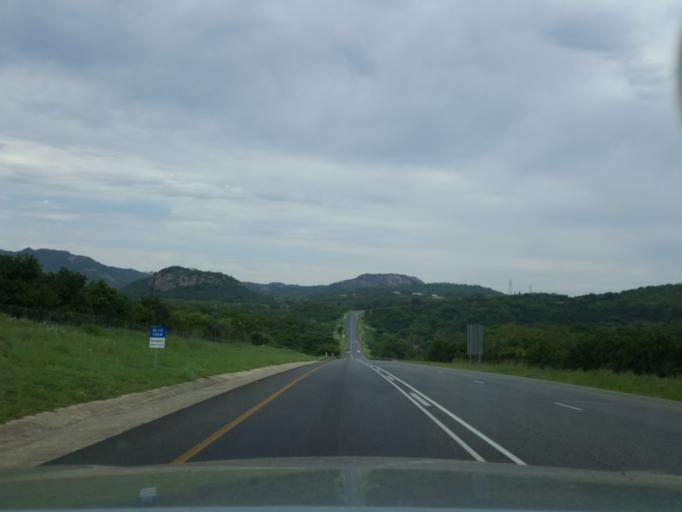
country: ZA
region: Mpumalanga
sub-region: Ehlanzeni District
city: Nelspruit
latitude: -25.4867
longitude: 31.1271
